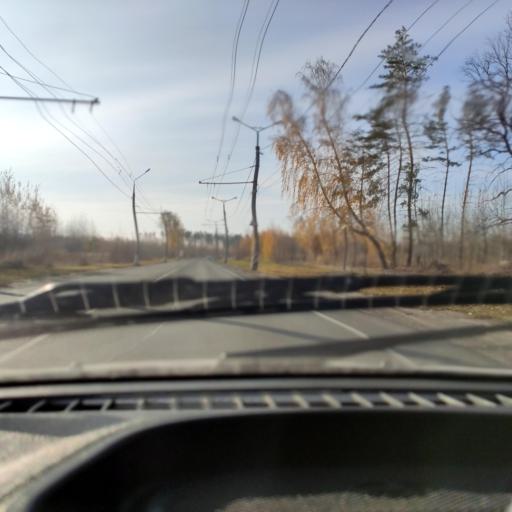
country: RU
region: Samara
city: Tol'yatti
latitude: 53.4849
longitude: 49.3806
